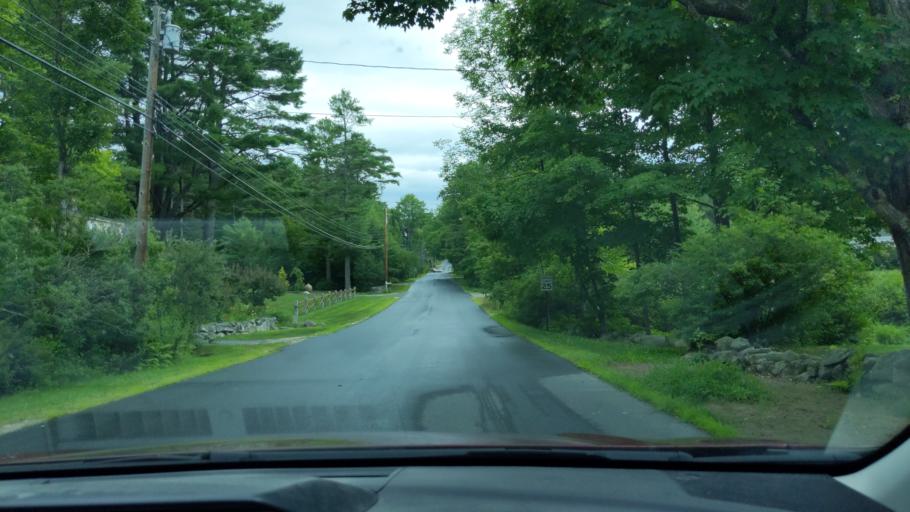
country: US
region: New Hampshire
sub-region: Merrimack County
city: New London
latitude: 43.4149
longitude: -72.0119
